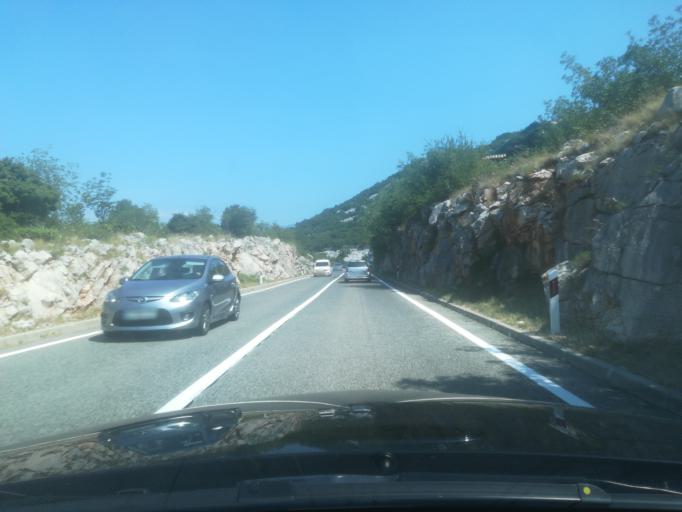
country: HR
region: Licko-Senjska
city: Senj
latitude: 44.8839
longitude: 14.9117
